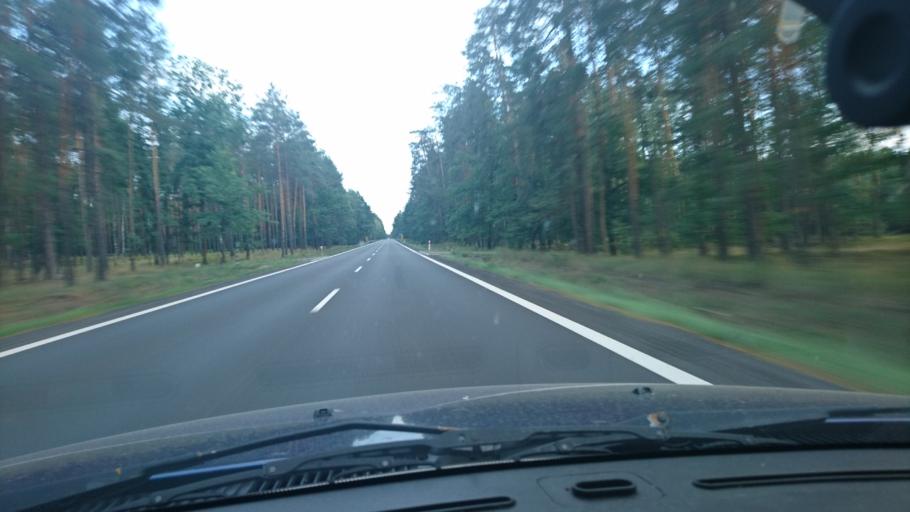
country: PL
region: Silesian Voivodeship
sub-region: Powiat tarnogorski
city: Tworog
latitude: 50.5644
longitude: 18.7126
